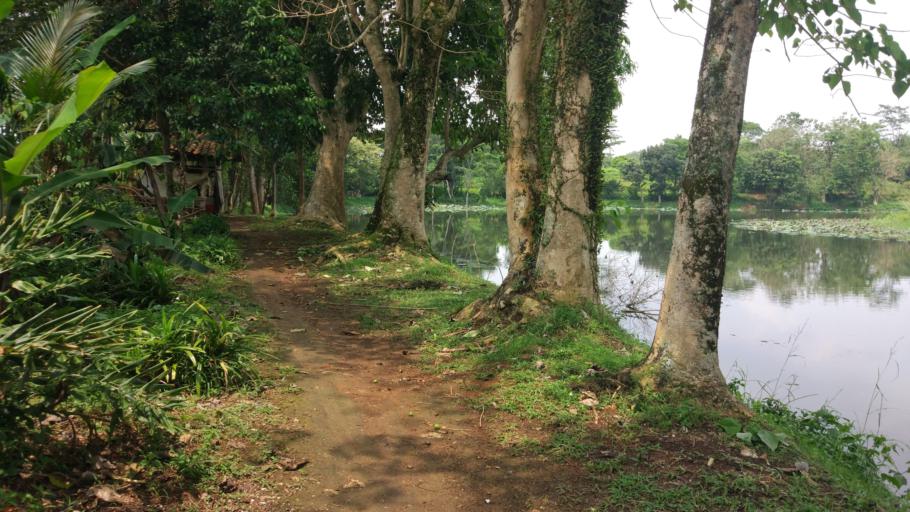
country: ID
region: West Java
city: Ciampea
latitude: -6.5470
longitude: 106.7329
